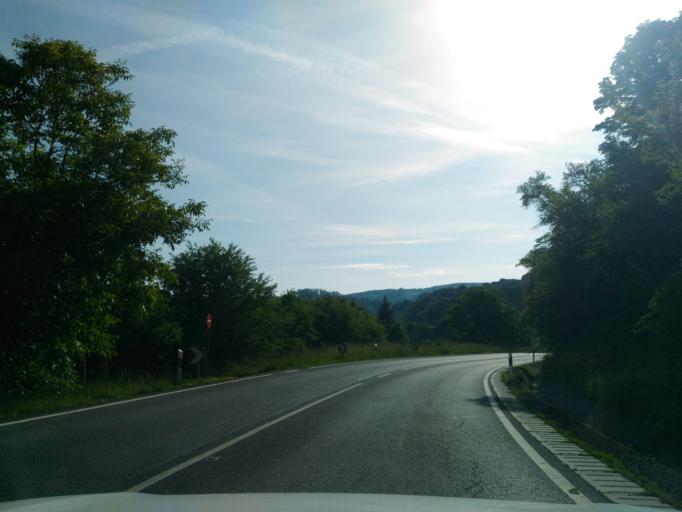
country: HU
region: Baranya
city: Komlo
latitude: 46.1598
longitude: 18.2430
